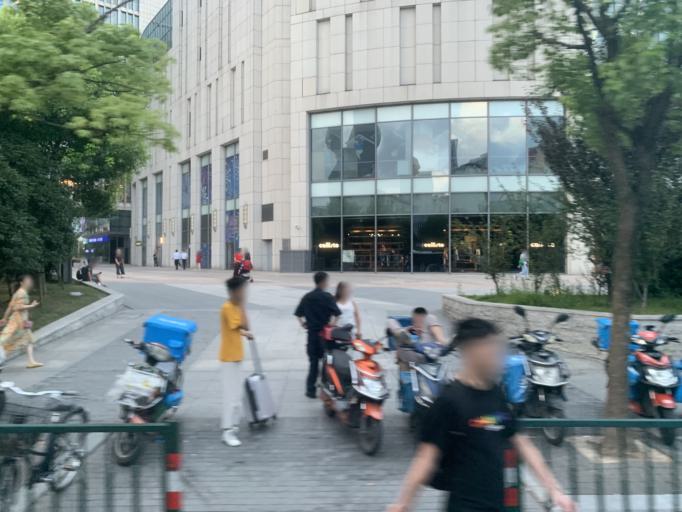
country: CN
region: Shanghai Shi
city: Pudong
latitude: 31.2324
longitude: 121.5242
